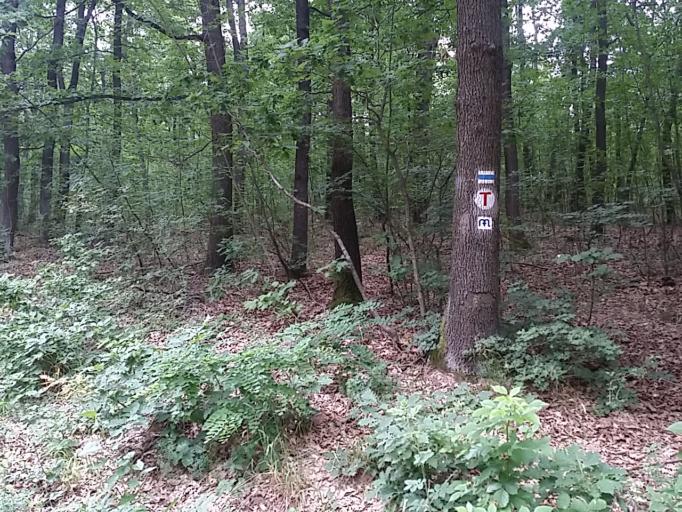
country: HU
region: Pest
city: Csobanka
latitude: 47.6501
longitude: 18.9431
